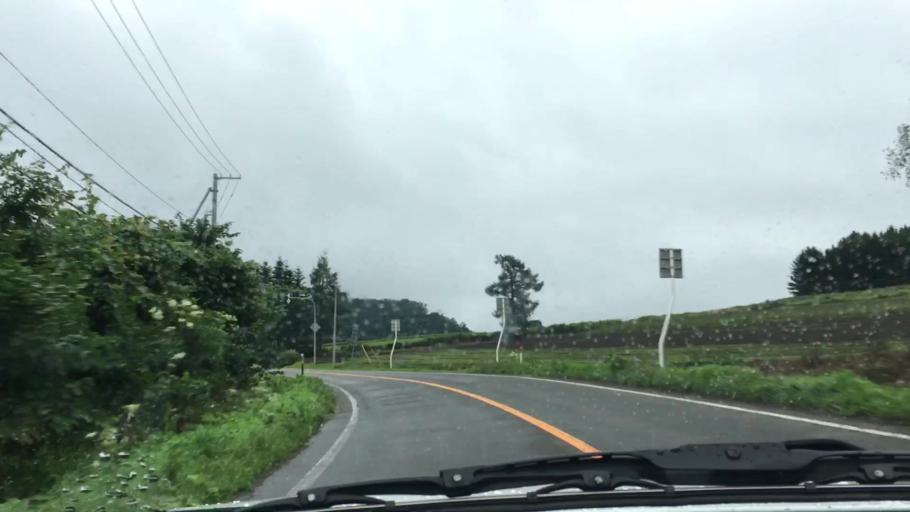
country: JP
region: Hokkaido
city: Niseko Town
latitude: 42.6109
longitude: 140.7267
